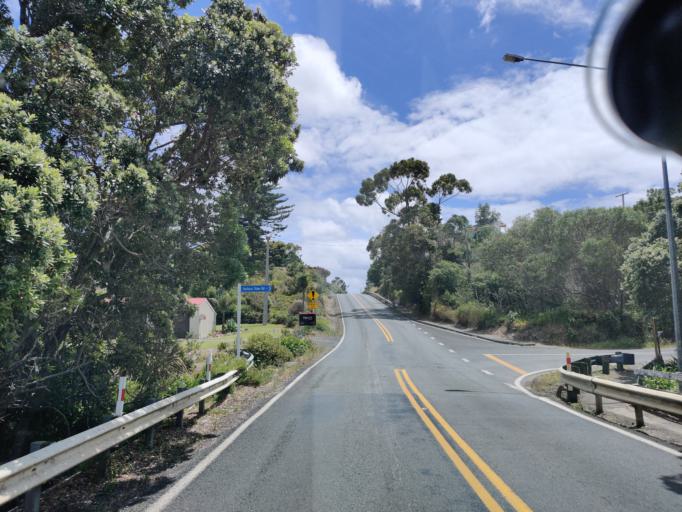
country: NZ
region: Northland
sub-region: Far North District
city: Kaitaia
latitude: -34.8112
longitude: 173.1163
